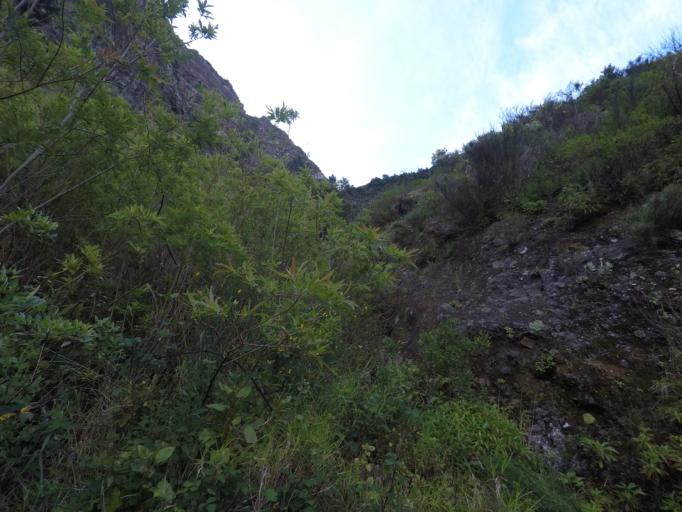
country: PT
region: Madeira
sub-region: Camara de Lobos
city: Curral das Freiras
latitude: 32.7126
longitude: -16.9629
